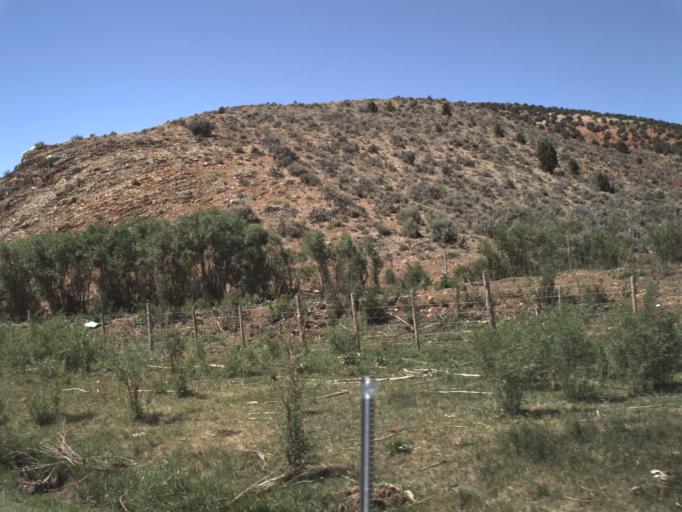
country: US
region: Utah
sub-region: Rich County
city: Randolph
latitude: 41.5014
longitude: -111.2805
